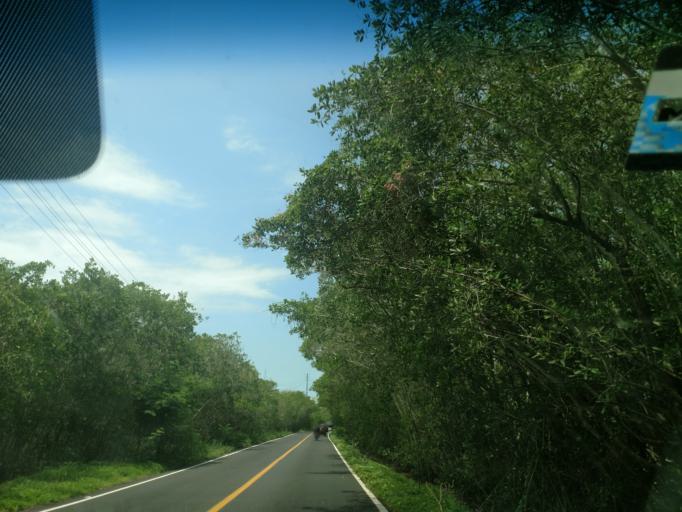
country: MX
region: Nayarit
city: San Blas
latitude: 21.5490
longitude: -105.2592
